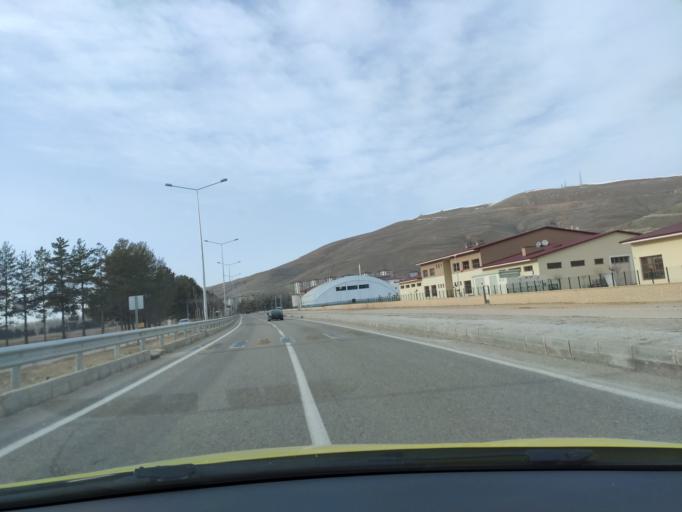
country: TR
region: Bayburt
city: Bayburt
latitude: 40.2334
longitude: 40.2557
